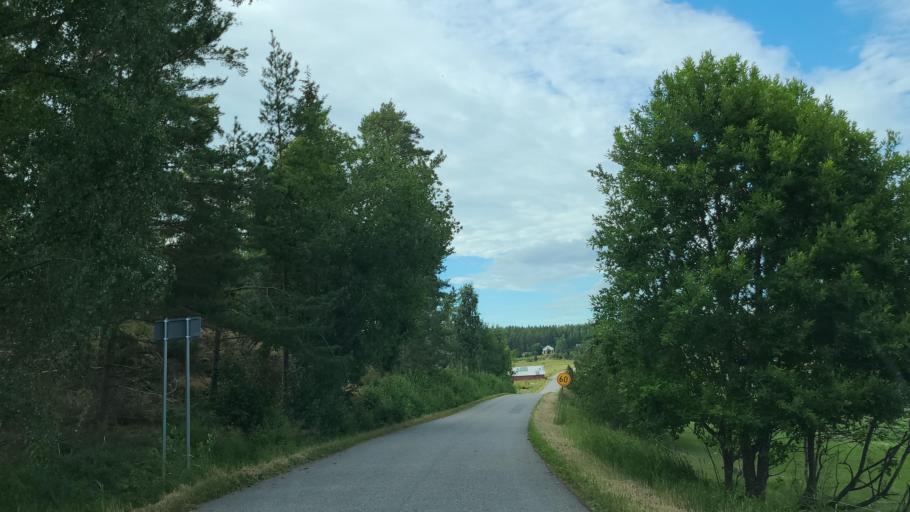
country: FI
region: Varsinais-Suomi
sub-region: Turku
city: Rymaettylae
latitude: 60.2942
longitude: 21.9372
